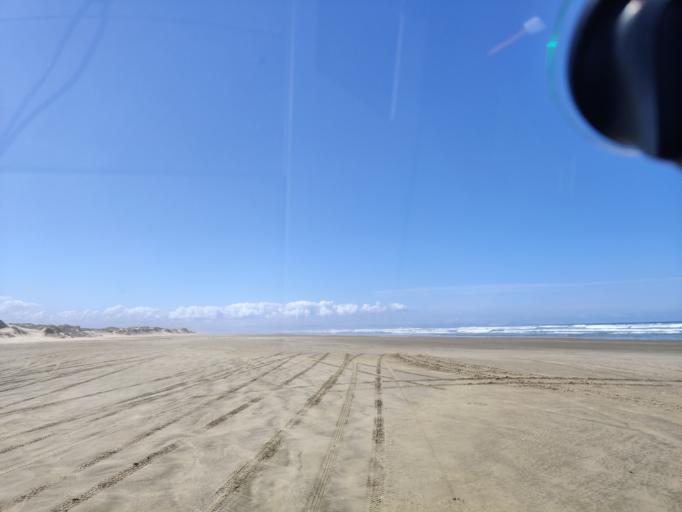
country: NZ
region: Northland
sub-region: Far North District
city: Ahipara
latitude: -34.8997
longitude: 173.0850
